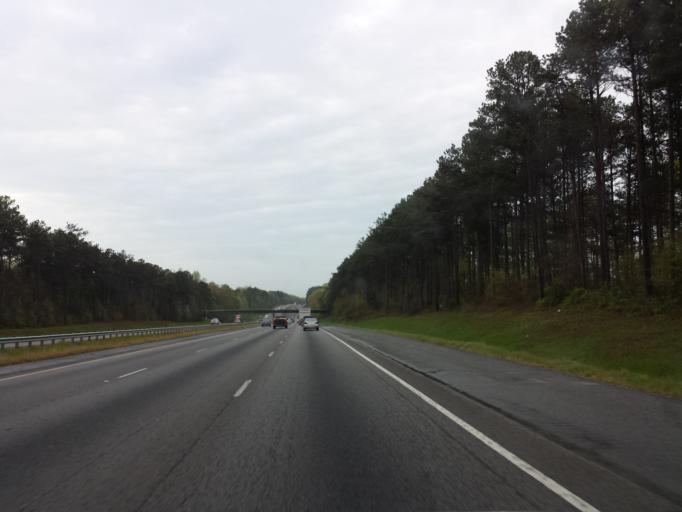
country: US
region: Georgia
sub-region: Henry County
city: Locust Grove
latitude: 33.3108
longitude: -84.1159
